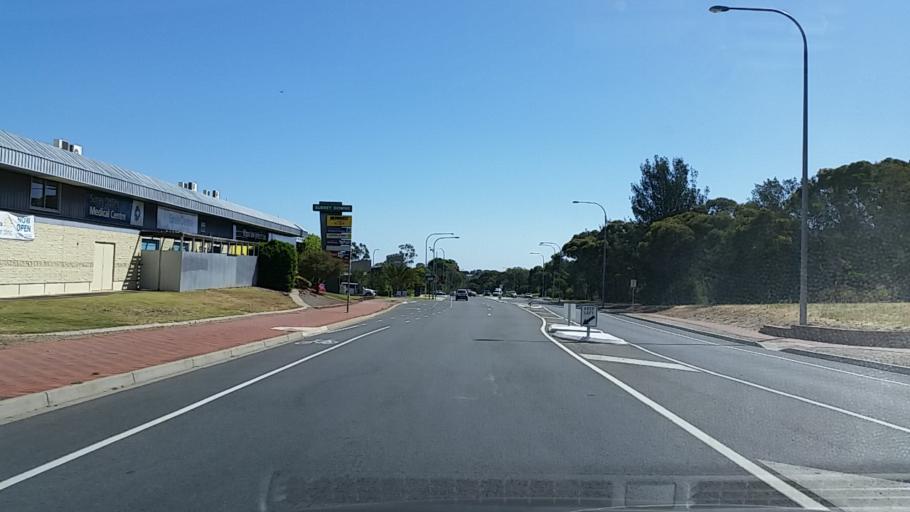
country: AU
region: South Australia
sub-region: Tea Tree Gully
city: Hope Valley
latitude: -34.8049
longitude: 138.7020
